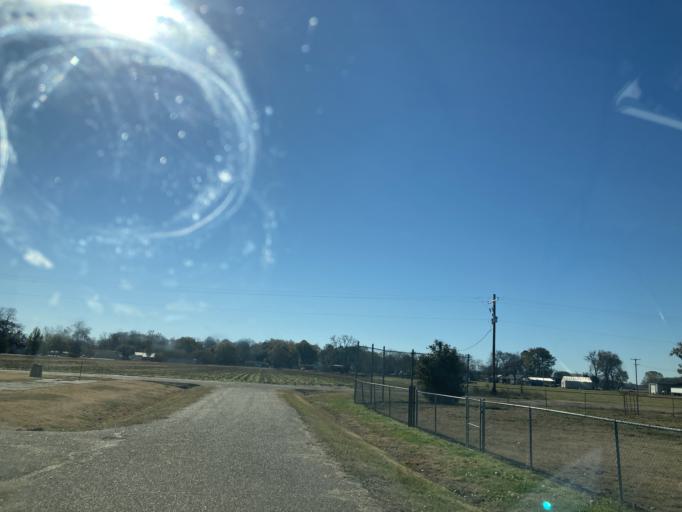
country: US
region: Mississippi
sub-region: Sharkey County
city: Rolling Fork
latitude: 32.8256
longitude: -90.7087
